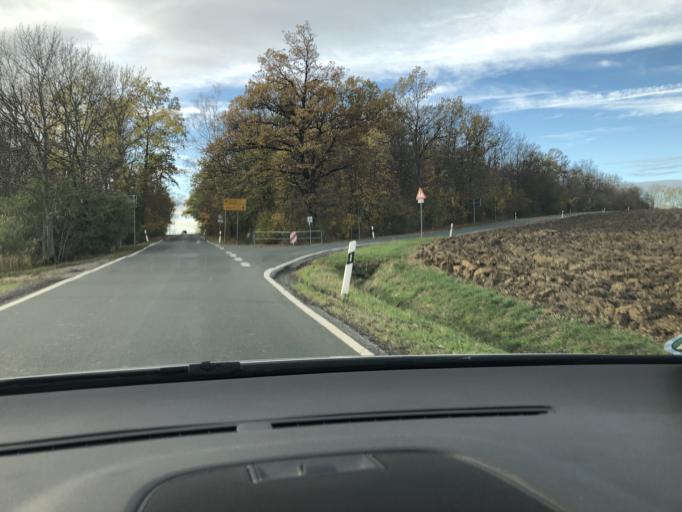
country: DE
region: Thuringia
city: Lehesten
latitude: 50.9601
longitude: 11.5666
